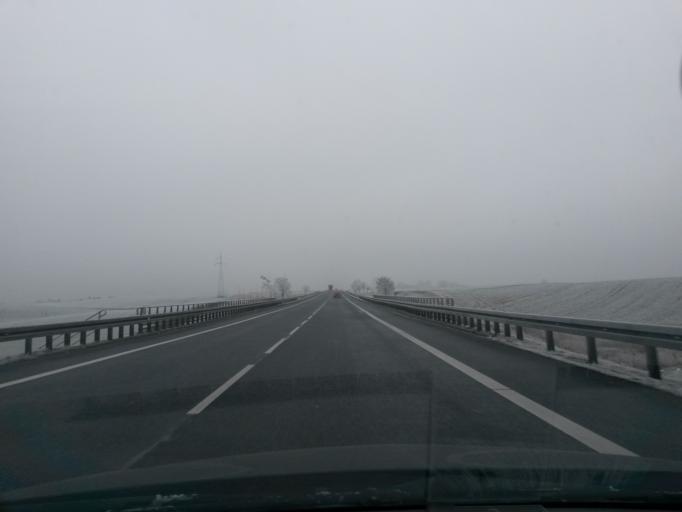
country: PL
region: Greater Poland Voivodeship
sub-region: Powiat gnieznienski
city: Gniezno
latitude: 52.5523
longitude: 17.6452
